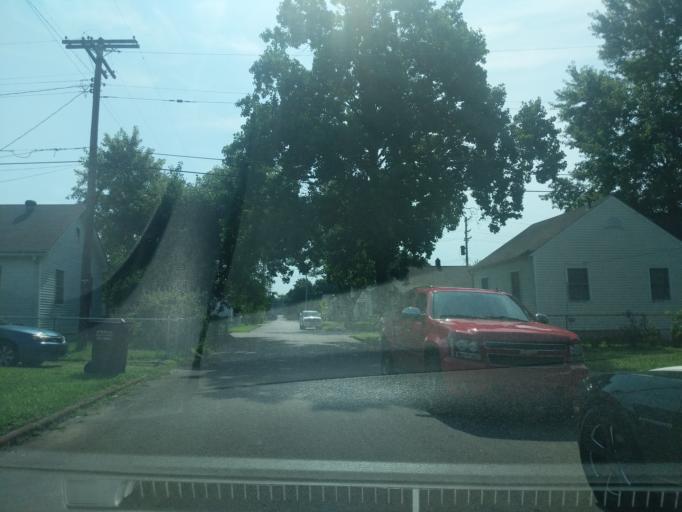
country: US
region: Tennessee
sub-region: Davidson County
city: Lakewood
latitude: 36.2608
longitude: -86.6508
